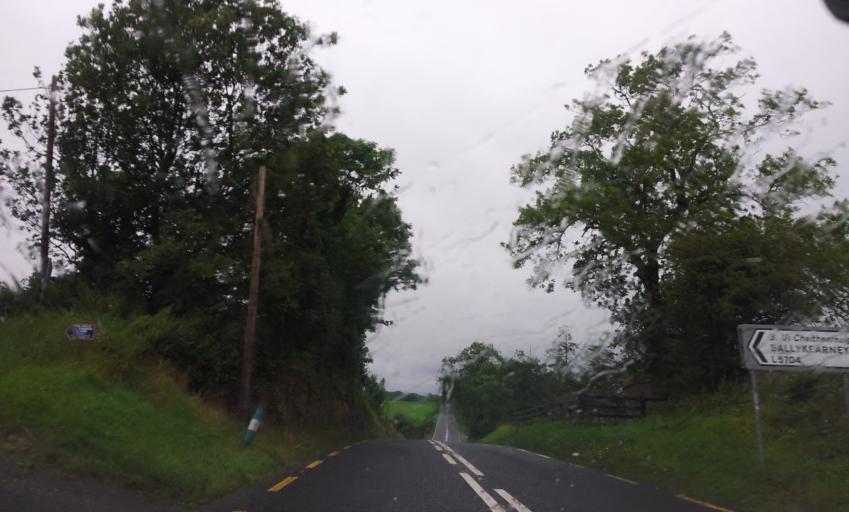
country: IE
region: Munster
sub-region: County Cork
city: Mitchelstown
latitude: 52.2638
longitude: -8.3054
